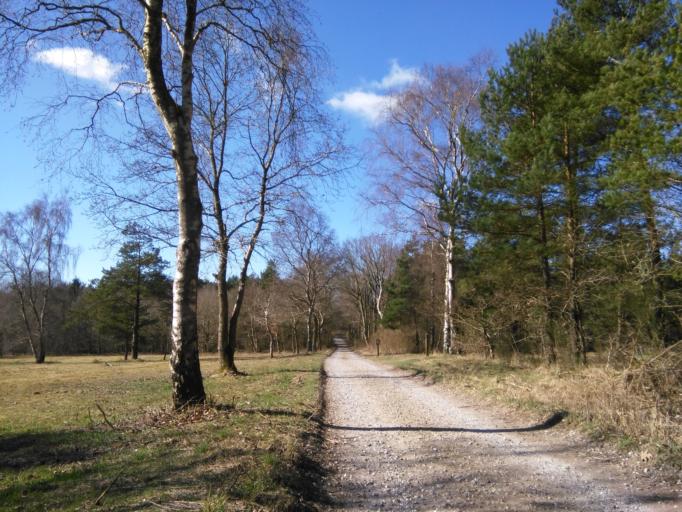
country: DK
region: Central Jutland
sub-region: Skanderborg Kommune
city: Ry
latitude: 56.0515
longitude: 9.7455
